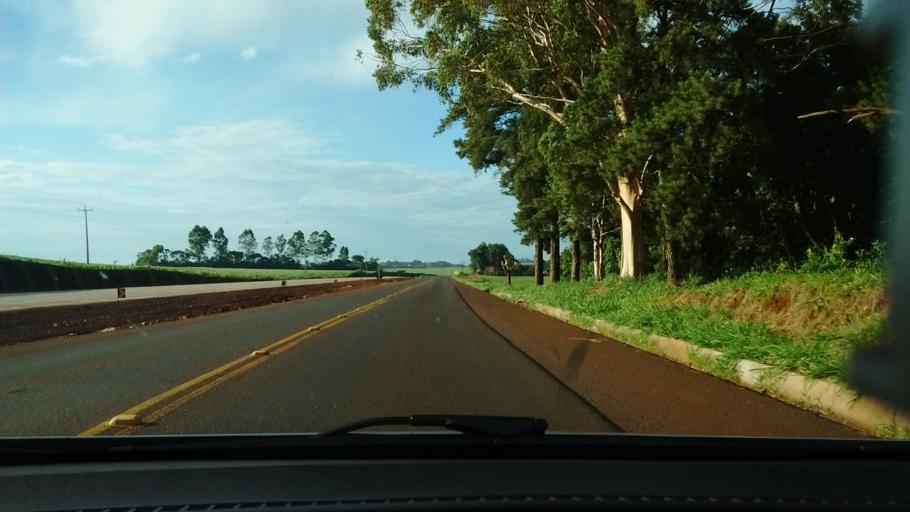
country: BR
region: Parana
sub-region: Cascavel
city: Cascavel
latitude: -25.1170
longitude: -53.5851
